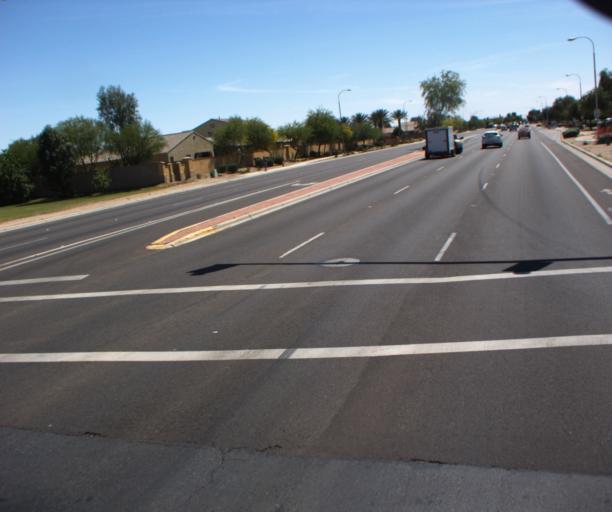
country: US
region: Arizona
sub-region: Maricopa County
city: Chandler
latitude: 33.2548
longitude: -111.8414
